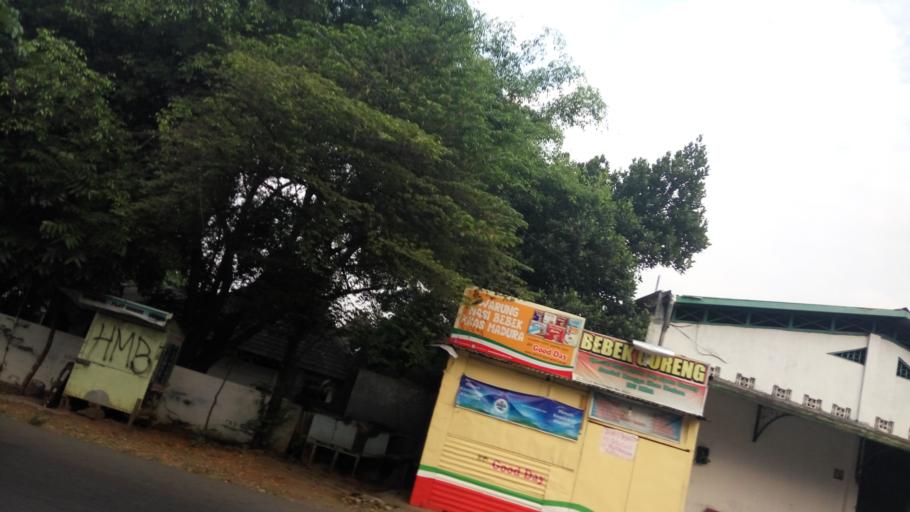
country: ID
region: Central Java
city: Semarang
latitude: -7.0049
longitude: 110.3914
